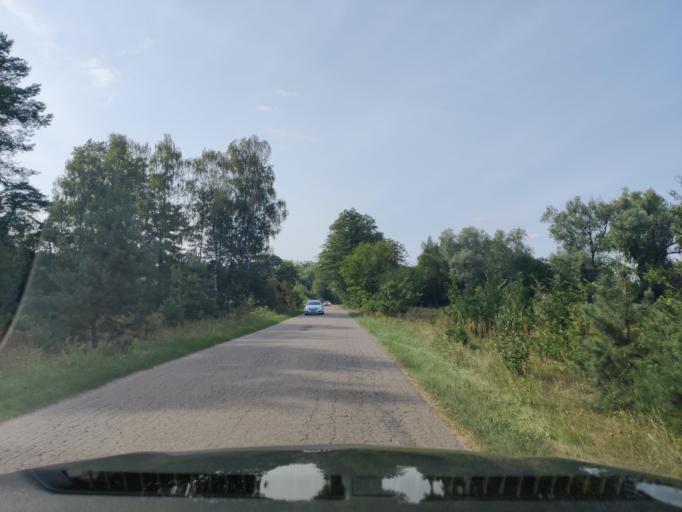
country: PL
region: Masovian Voivodeship
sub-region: Powiat wyszkowski
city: Rzasnik
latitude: 52.7428
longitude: 21.3208
